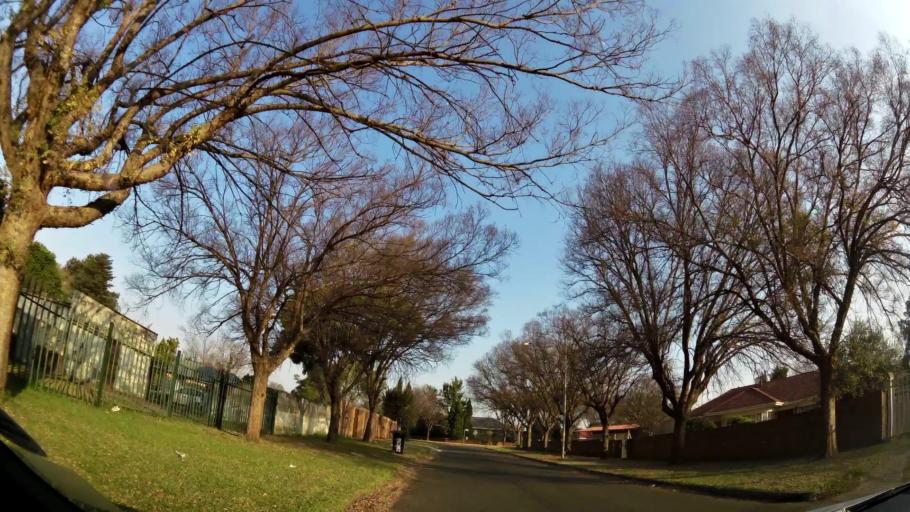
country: ZA
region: Gauteng
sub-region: Ekurhuleni Metropolitan Municipality
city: Springs
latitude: -26.2944
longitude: 28.4480
